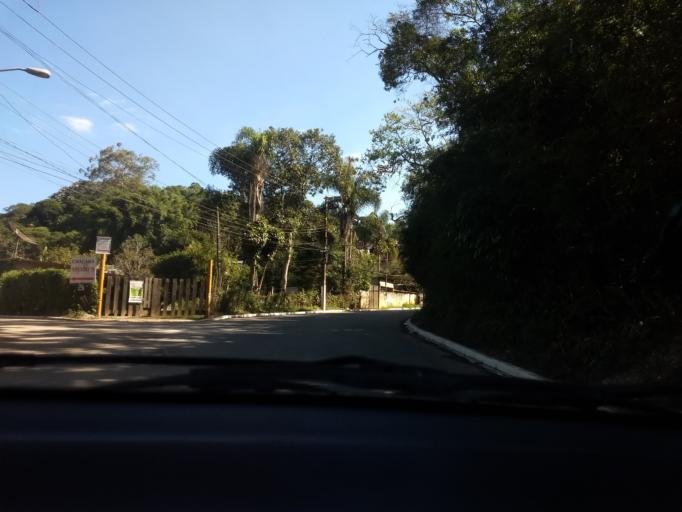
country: BR
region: Sao Paulo
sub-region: Embu-Guacu
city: Embu Guacu
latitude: -23.8090
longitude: -46.7459
